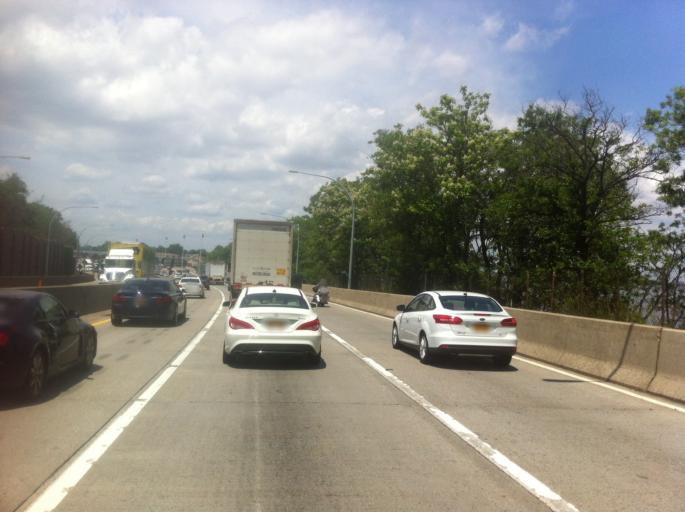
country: US
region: New York
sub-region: Nassau County
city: East Atlantic Beach
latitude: 40.8153
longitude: -73.7967
